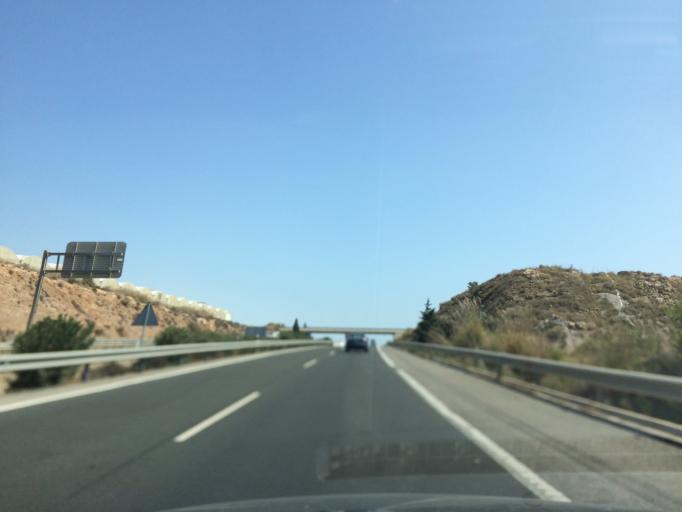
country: ES
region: Andalusia
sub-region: Provincia de Almeria
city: Adra
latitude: 36.7688
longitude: -2.9788
